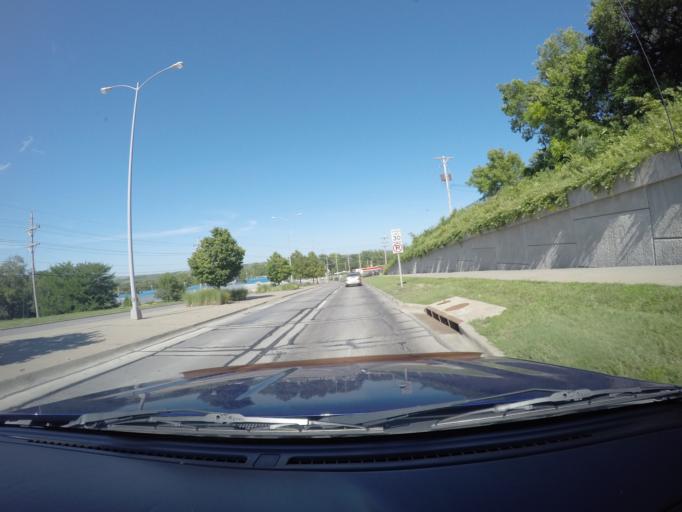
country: US
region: Kansas
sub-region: Riley County
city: Manhattan
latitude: 39.2069
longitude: -96.5740
